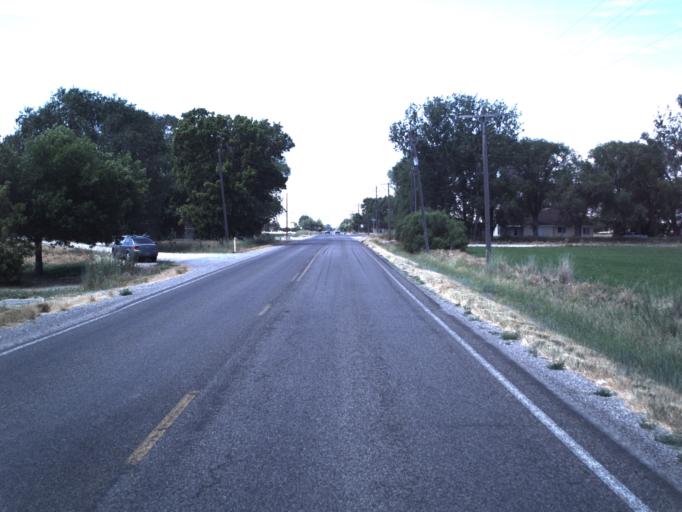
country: US
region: Utah
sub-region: Box Elder County
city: Tremonton
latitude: 41.7106
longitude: -112.2181
